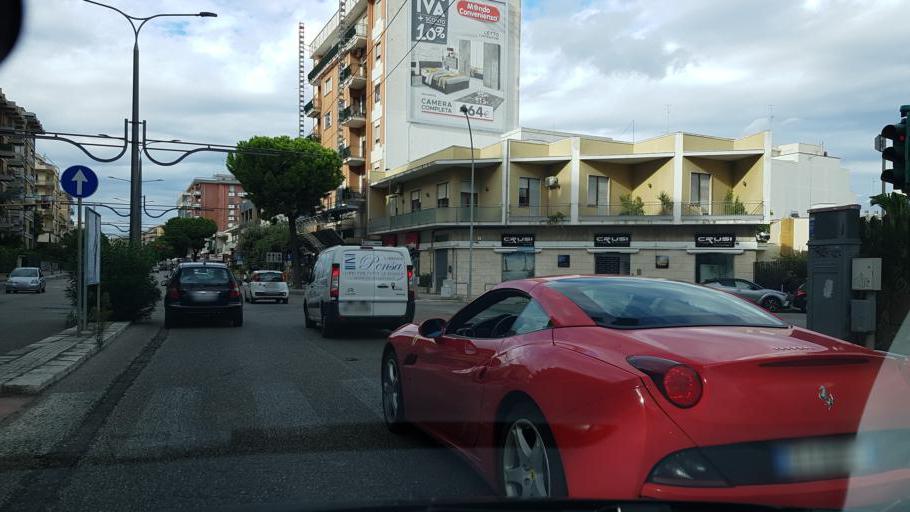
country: IT
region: Apulia
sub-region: Provincia di Lecce
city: Lecce
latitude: 40.3533
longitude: 18.1858
